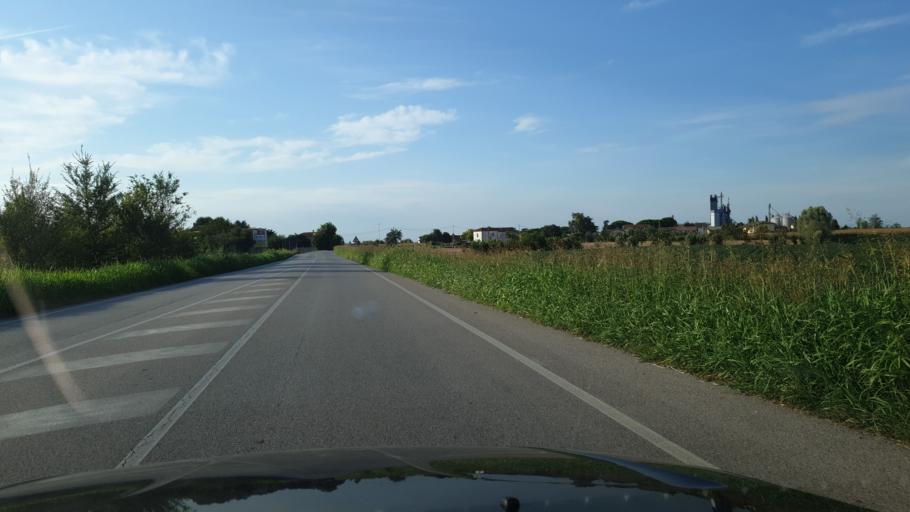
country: IT
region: Veneto
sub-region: Provincia di Rovigo
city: Fiesso Umbertiano
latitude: 44.9663
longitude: 11.6119
